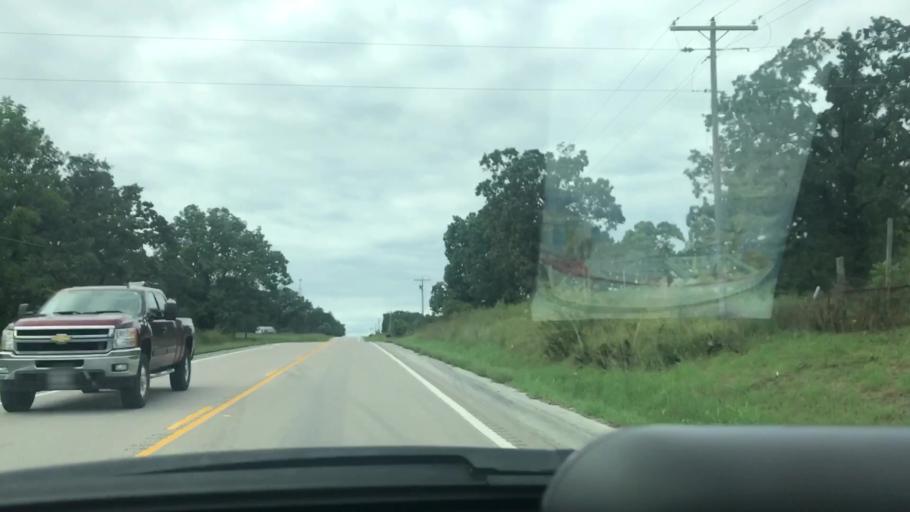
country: US
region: Missouri
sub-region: Benton County
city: Warsaw
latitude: 38.1383
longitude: -93.2848
